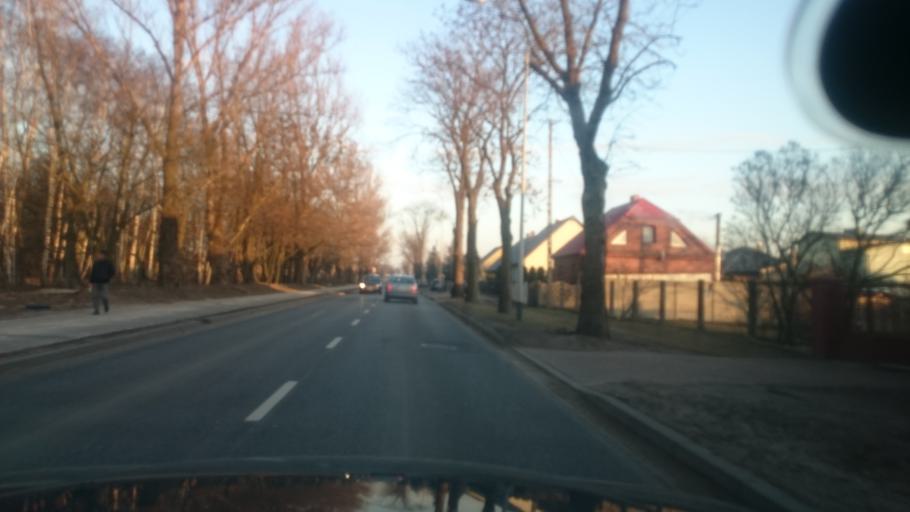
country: PL
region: Greater Poland Voivodeship
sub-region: Powiat ostrowski
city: Ostrow Wielkopolski
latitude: 51.6458
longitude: 17.8563
